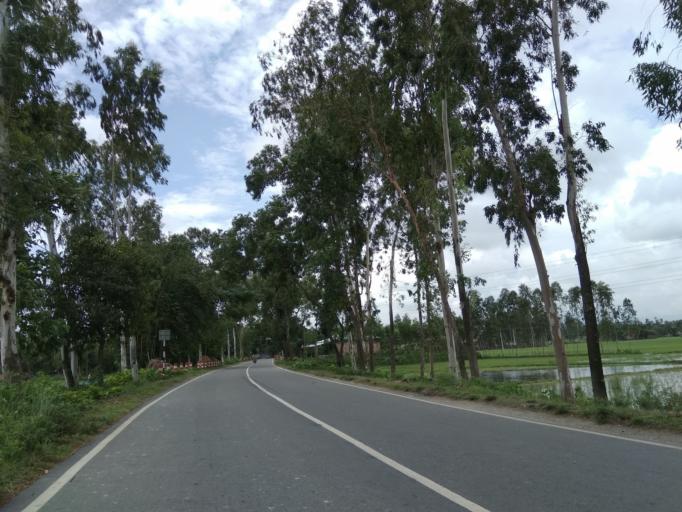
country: BD
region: Rajshahi
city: Saidpur
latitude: 25.7701
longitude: 88.8047
